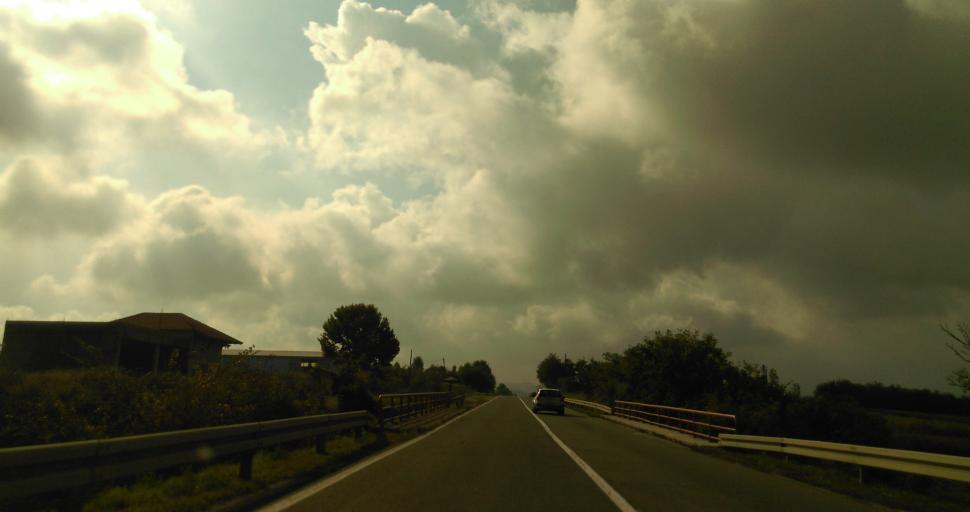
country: RS
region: Central Serbia
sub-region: Kolubarski Okrug
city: Ljig
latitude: 44.2647
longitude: 20.2854
